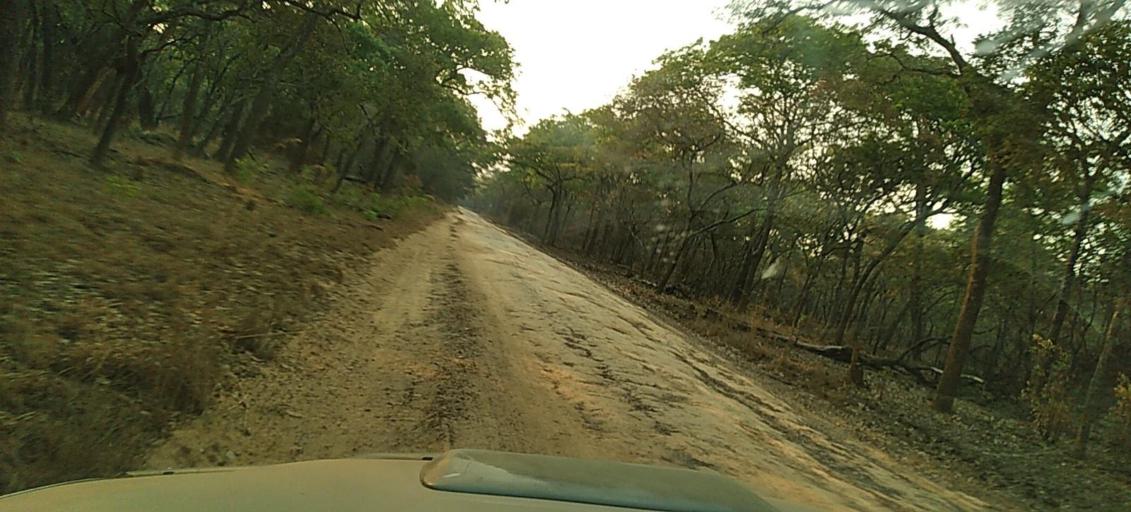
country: ZM
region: North-Western
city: Kasempa
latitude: -13.1574
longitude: 26.4478
